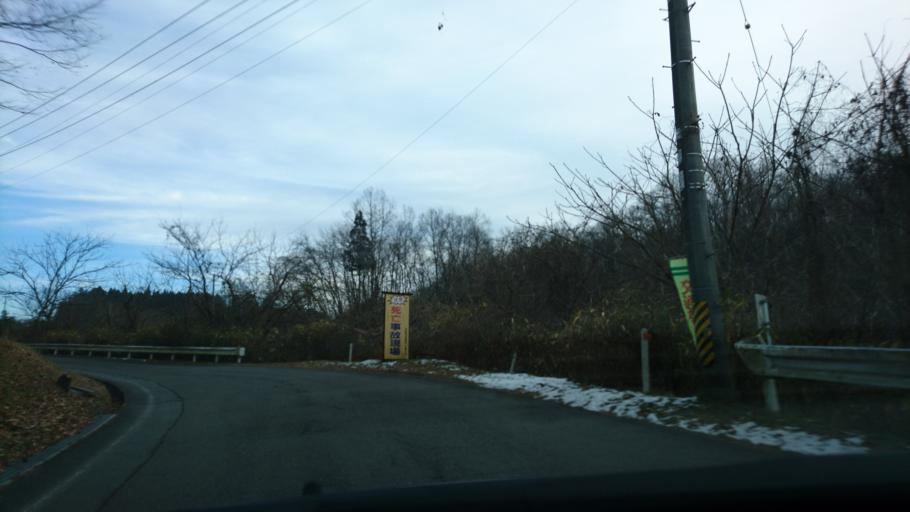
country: JP
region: Iwate
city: Ichinoseki
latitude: 38.9059
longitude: 141.3327
